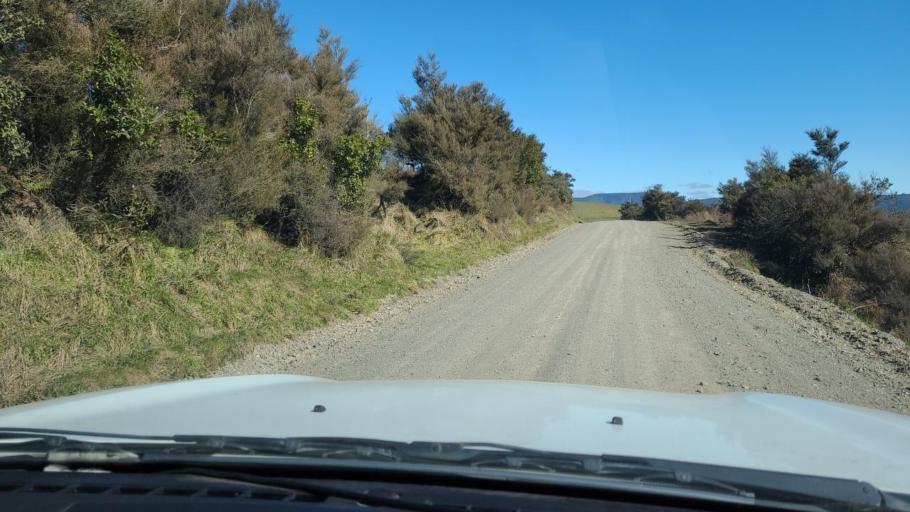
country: NZ
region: Hawke's Bay
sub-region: Napier City
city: Taradale
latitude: -39.4688
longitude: 176.4158
